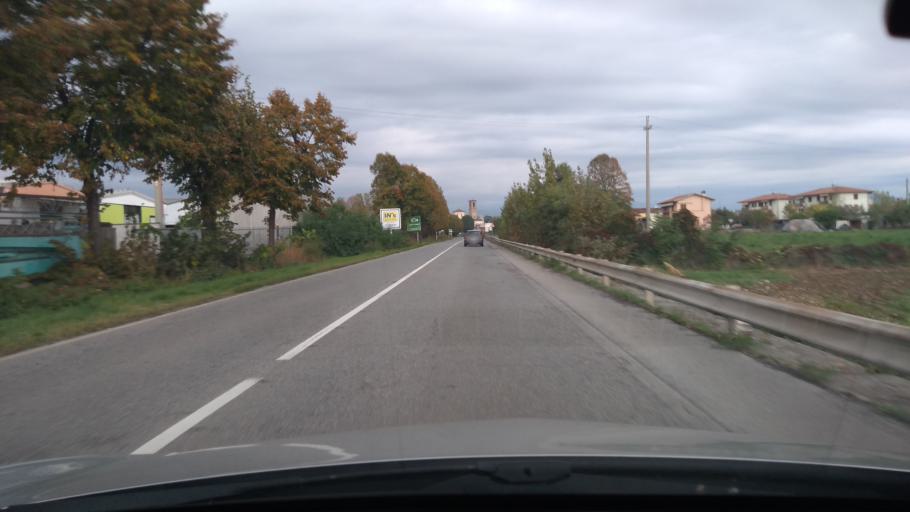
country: IT
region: Lombardy
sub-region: Provincia di Bergamo
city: Verdello
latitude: 45.5986
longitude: 9.6238
